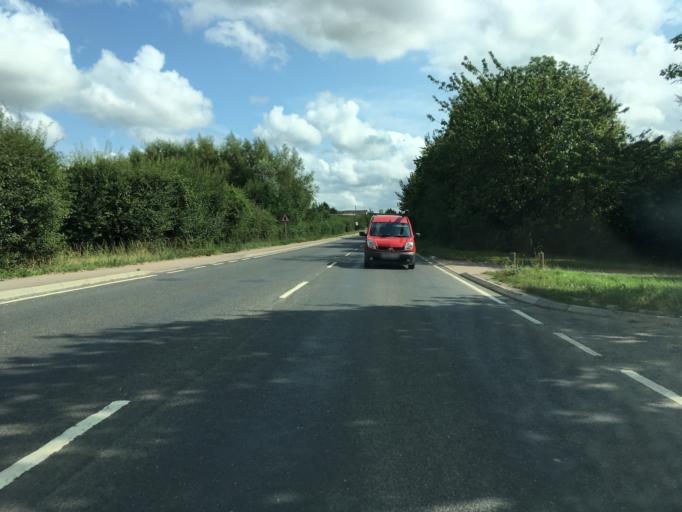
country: GB
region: England
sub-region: Kent
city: Headcorn
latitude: 51.2031
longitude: 0.5931
